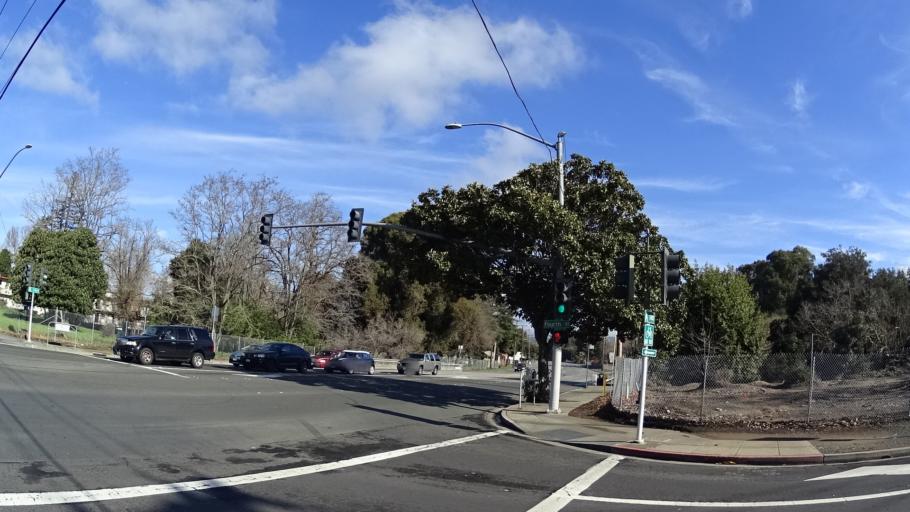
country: US
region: California
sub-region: Alameda County
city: Hayward
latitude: 37.6785
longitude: -122.0772
